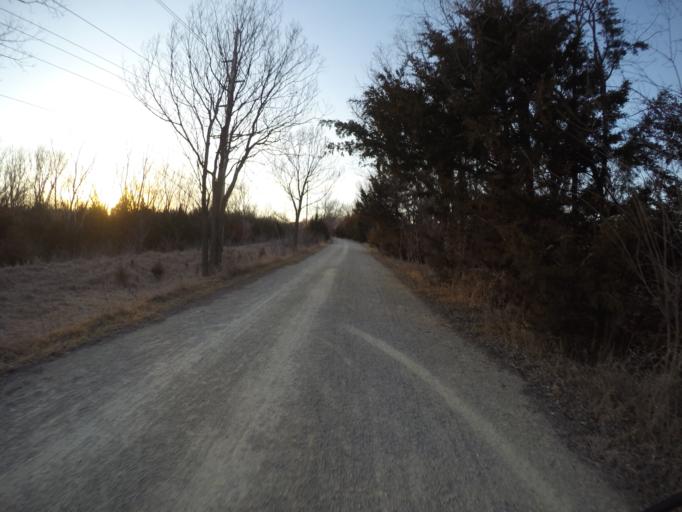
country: US
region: Kansas
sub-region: Riley County
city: Manhattan
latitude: 39.1869
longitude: -96.6138
